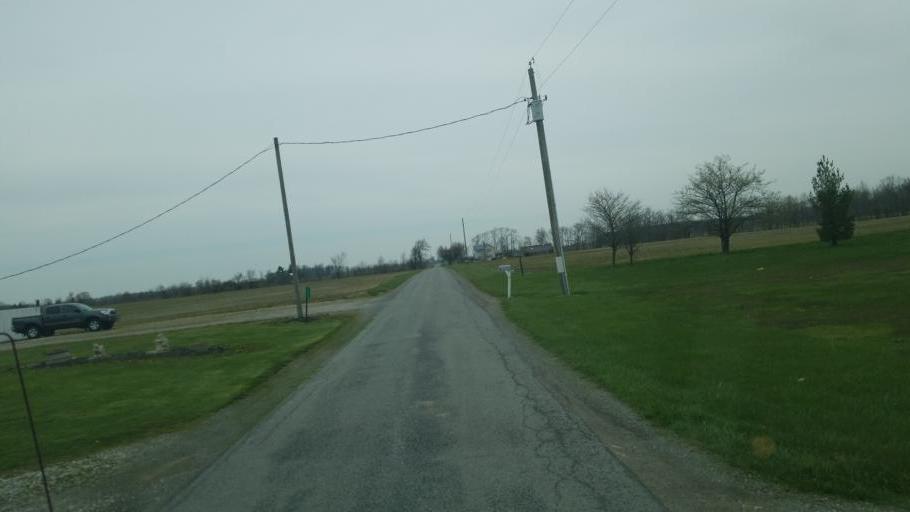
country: US
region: Ohio
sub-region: Hardin County
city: Forest
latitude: 40.8975
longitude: -83.5149
